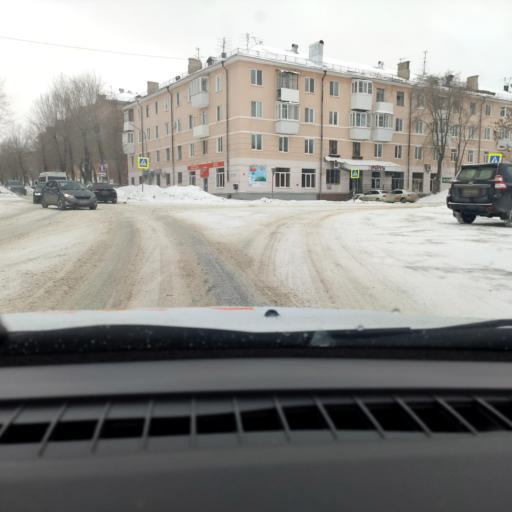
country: RU
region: Samara
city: Novokuybyshevsk
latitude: 53.0976
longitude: 49.9460
